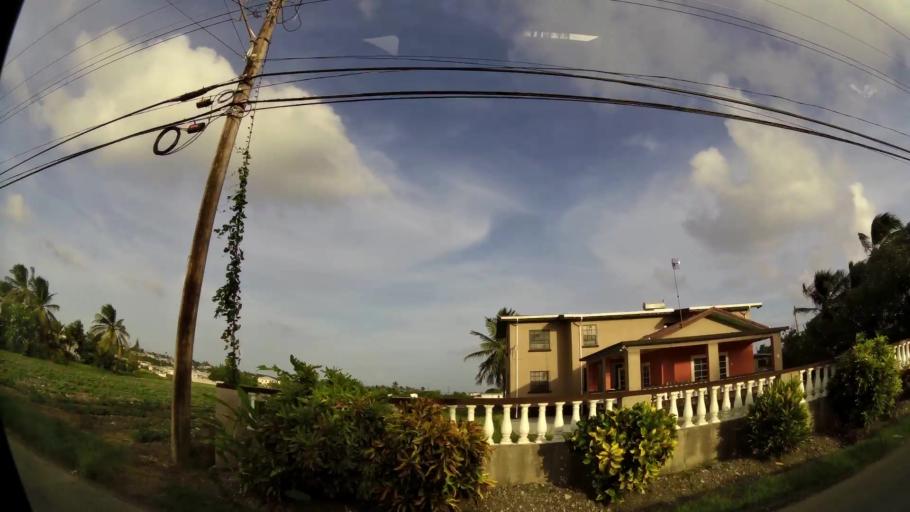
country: BB
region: Christ Church
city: Oistins
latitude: 13.0626
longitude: -59.5090
